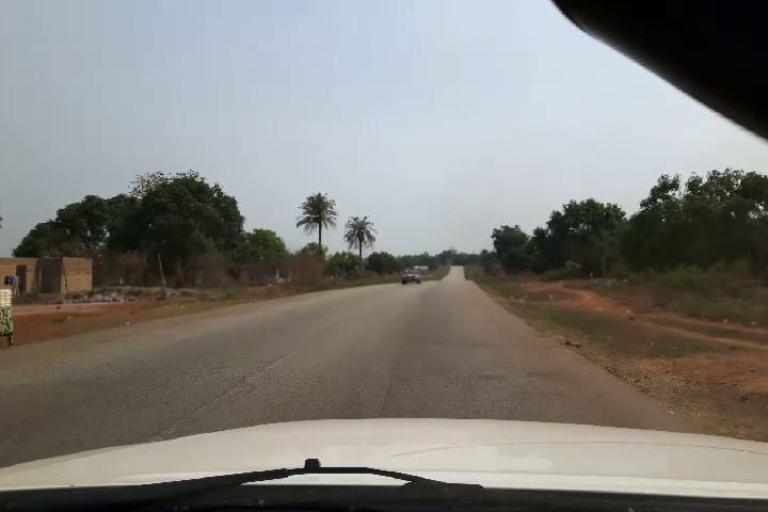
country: SL
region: Southern Province
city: Largo
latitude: 8.3152
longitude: -12.2176
